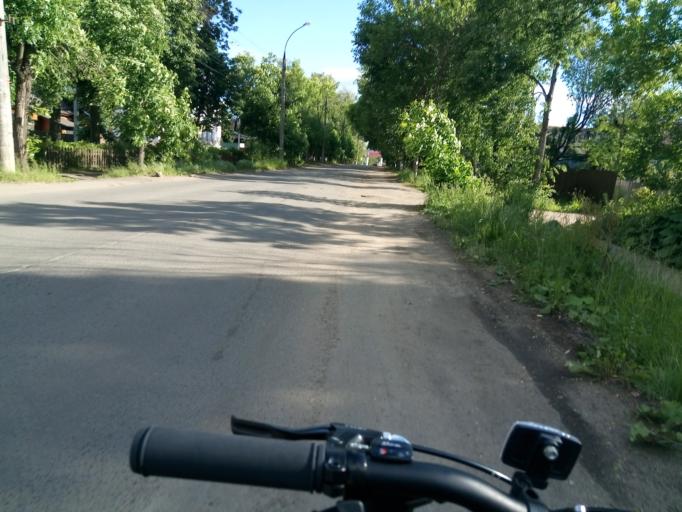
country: RU
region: Jaroslavl
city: Yaroslavl
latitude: 57.6400
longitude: 39.9124
